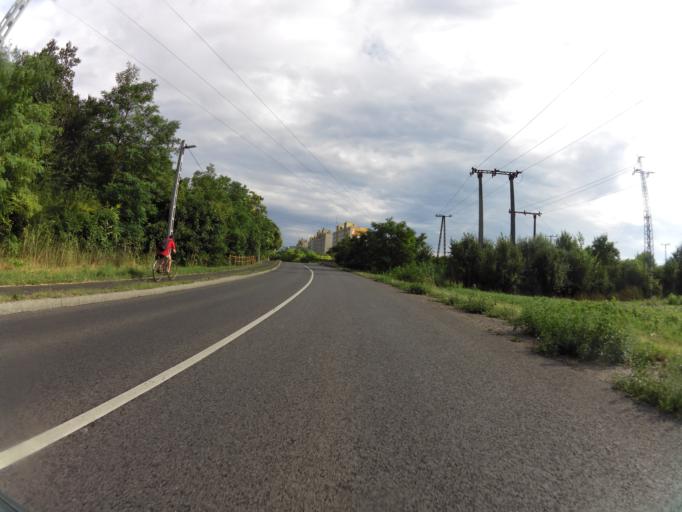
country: HU
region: Csongrad
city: Szeged
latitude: 46.2789
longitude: 20.1440
